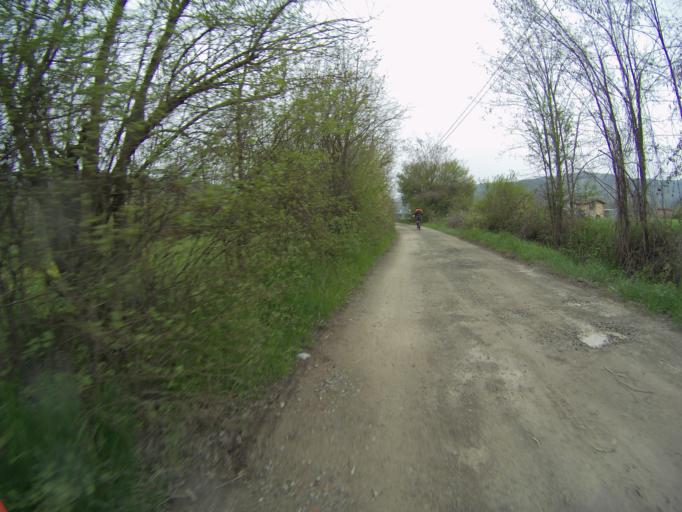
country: IT
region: Emilia-Romagna
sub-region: Provincia di Reggio Emilia
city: Ciano d'Enza
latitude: 44.5926
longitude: 10.4048
